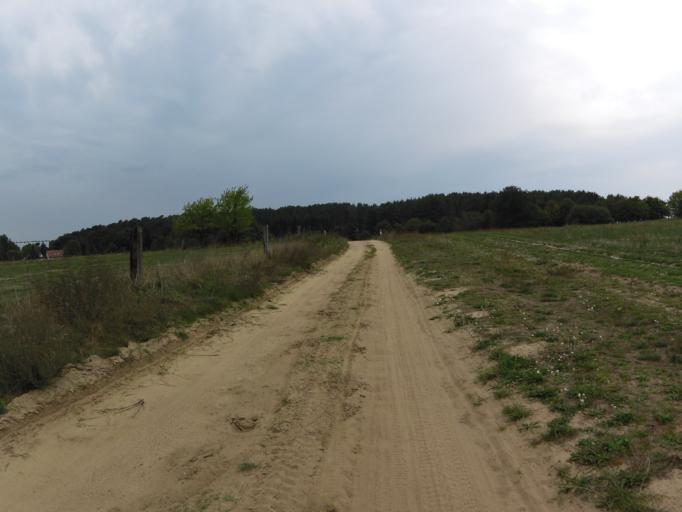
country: DE
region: Mecklenburg-Vorpommern
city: Seebad Heringsdorf
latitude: 53.9426
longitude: 14.1457
